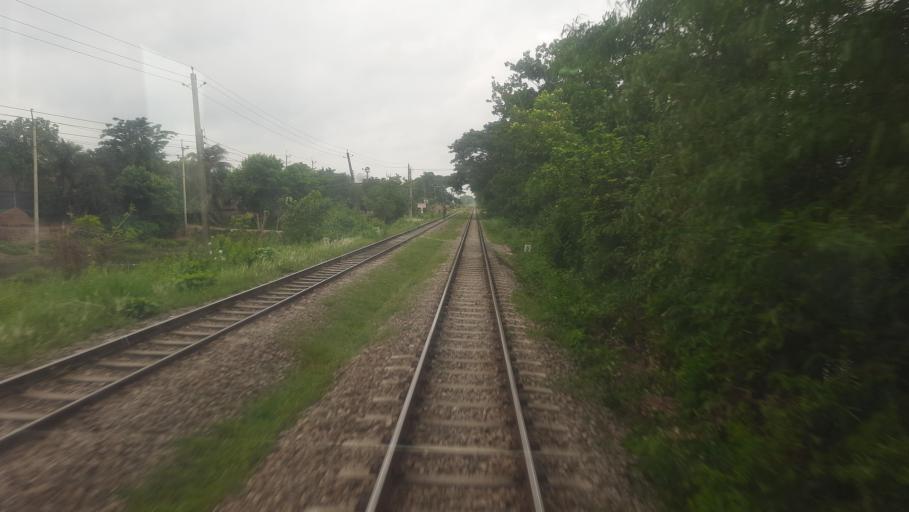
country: BD
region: Dhaka
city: Bhairab Bazar
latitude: 23.9843
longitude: 91.0723
